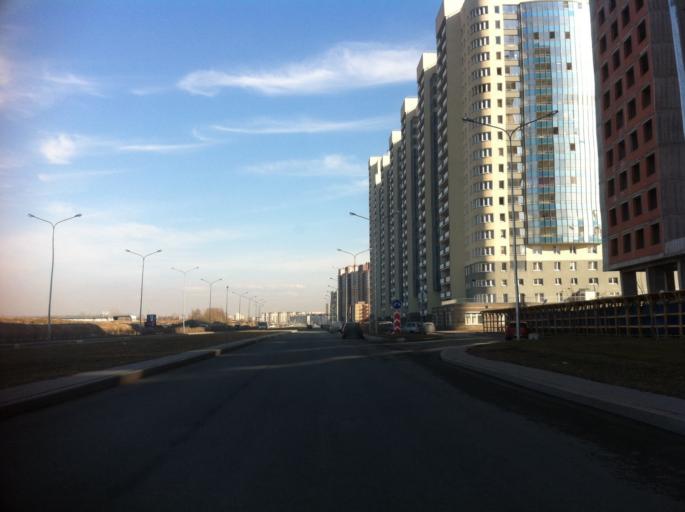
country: RU
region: St.-Petersburg
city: Uritsk
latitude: 59.8669
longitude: 30.1757
